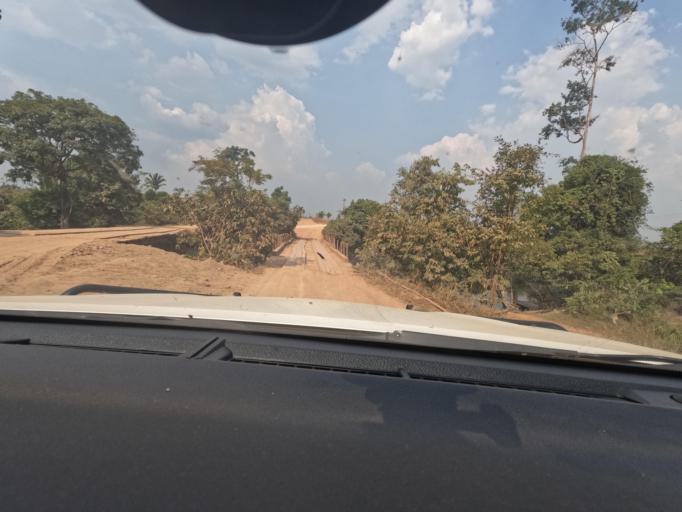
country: BR
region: Rondonia
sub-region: Porto Velho
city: Porto Velho
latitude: -8.6830
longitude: -63.1815
